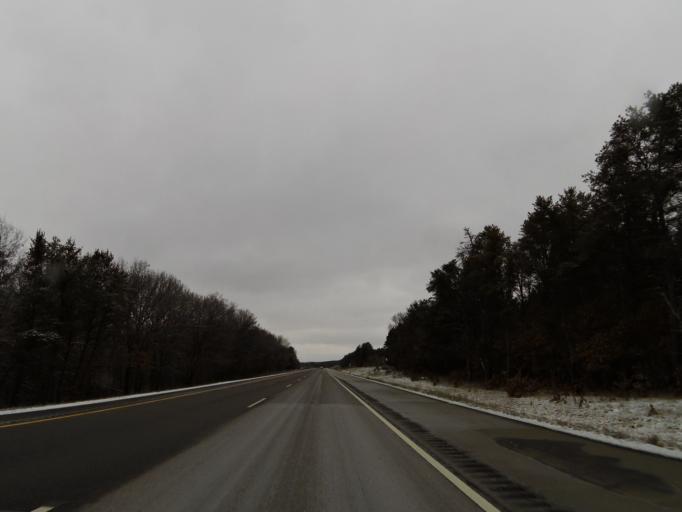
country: US
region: Wisconsin
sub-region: Trempealeau County
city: Osseo
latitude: 44.5520
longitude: -91.1681
